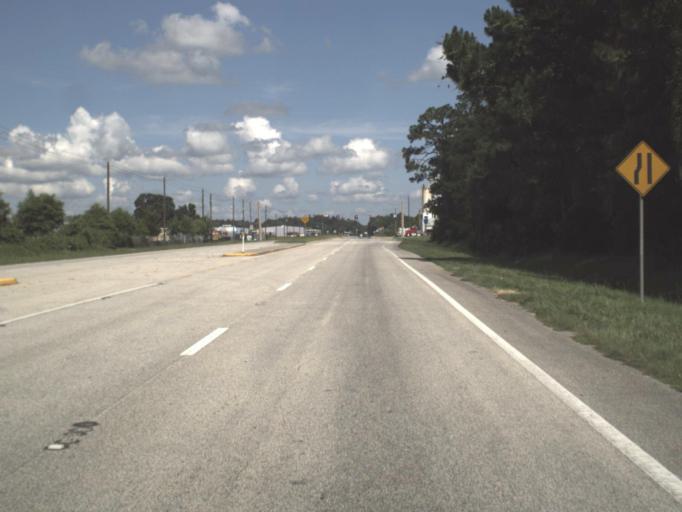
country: US
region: Florida
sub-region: Putnam County
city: Palatka
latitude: 29.6625
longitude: -81.6812
